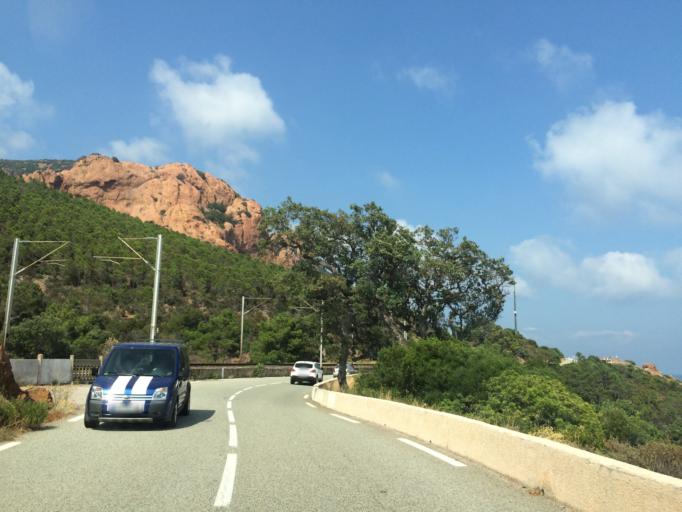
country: FR
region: Provence-Alpes-Cote d'Azur
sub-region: Departement des Alpes-Maritimes
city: Theoule-sur-Mer
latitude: 43.4431
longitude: 6.8999
